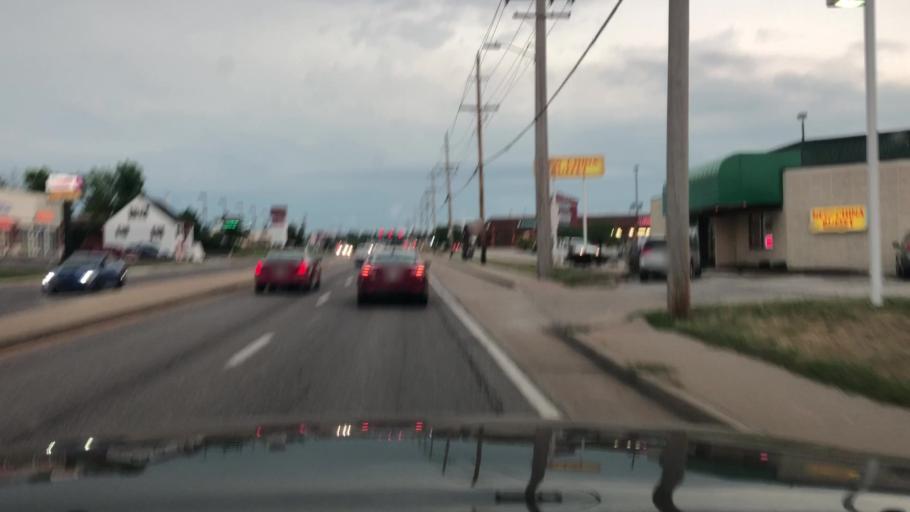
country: US
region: Missouri
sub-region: Saint Louis County
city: Bridgeton
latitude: 38.7507
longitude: -90.4259
